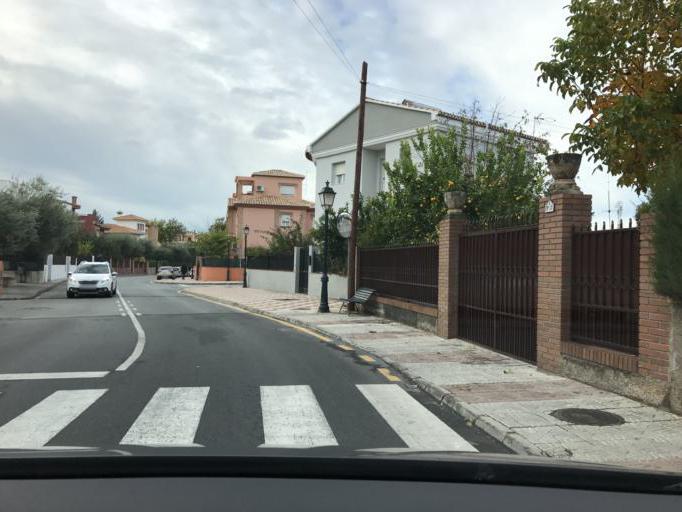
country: ES
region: Andalusia
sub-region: Provincia de Granada
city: Cajar
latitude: 37.1369
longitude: -3.5711
